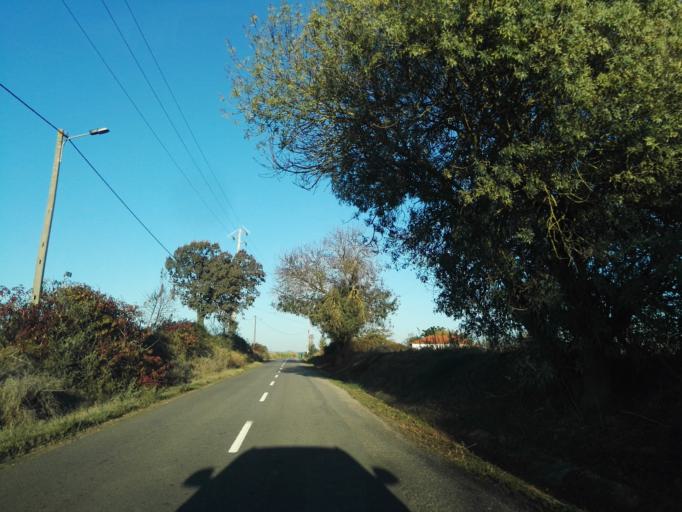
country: PT
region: Santarem
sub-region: Alpiarca
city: Alpiarca
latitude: 39.3463
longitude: -8.5600
